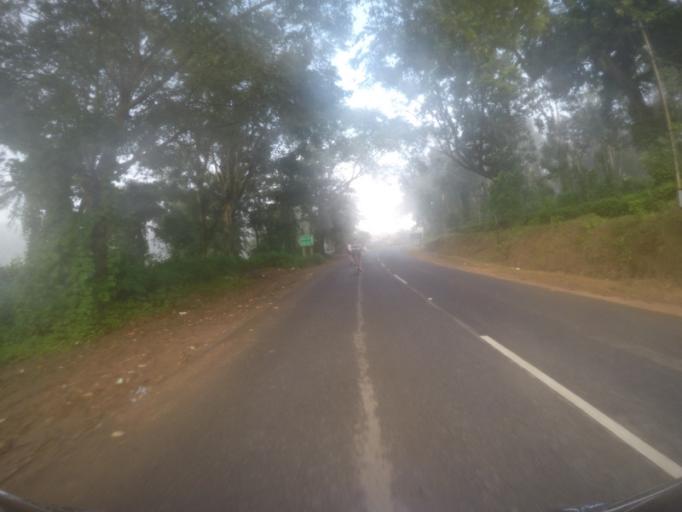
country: IN
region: Karnataka
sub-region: Kodagu
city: Suntikoppa
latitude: 12.4465
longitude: 75.8204
